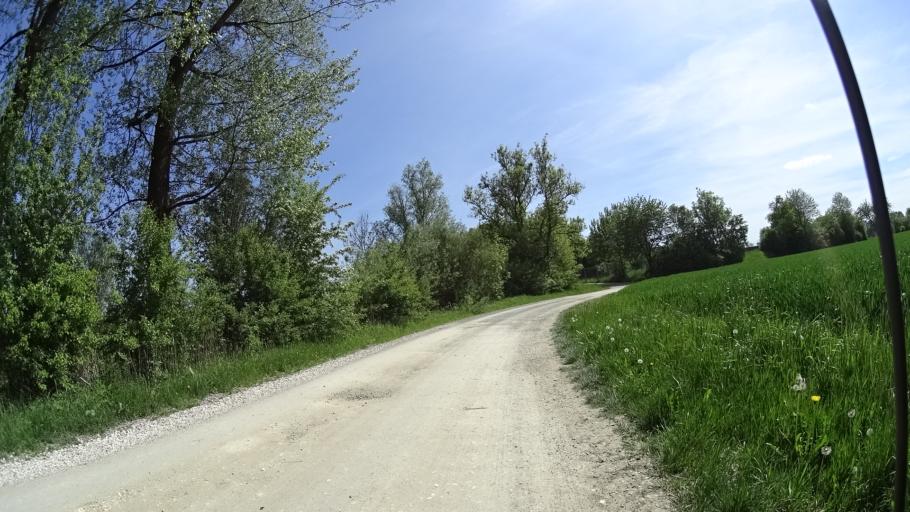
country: DE
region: Bavaria
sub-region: Swabia
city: Weissenhorn
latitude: 48.3219
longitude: 10.1487
